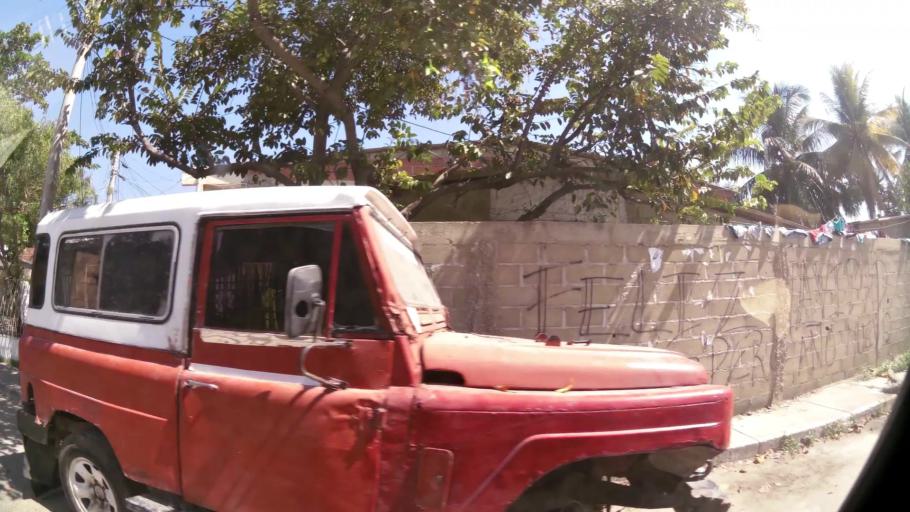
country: CO
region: Bolivar
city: Cartagena
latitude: 10.4366
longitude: -75.5166
